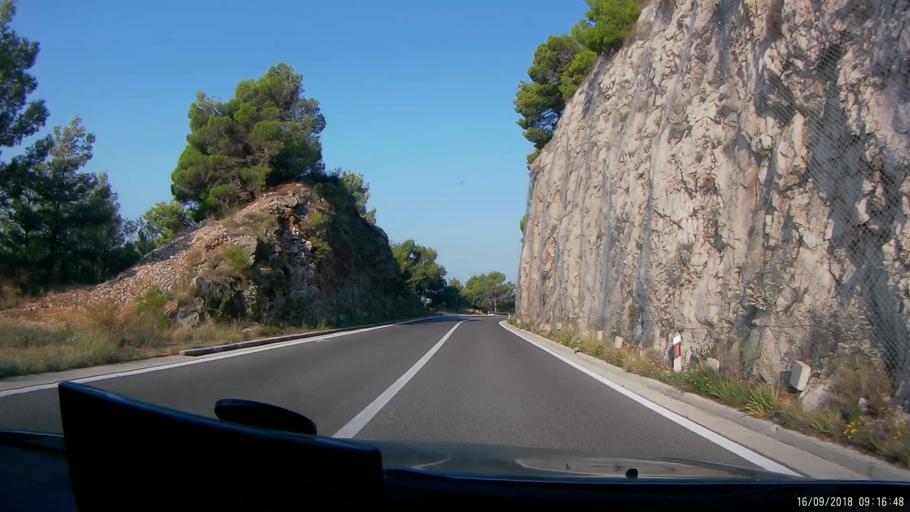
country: HR
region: Splitsko-Dalmatinska
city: Donja Brela
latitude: 43.4018
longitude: 16.8632
